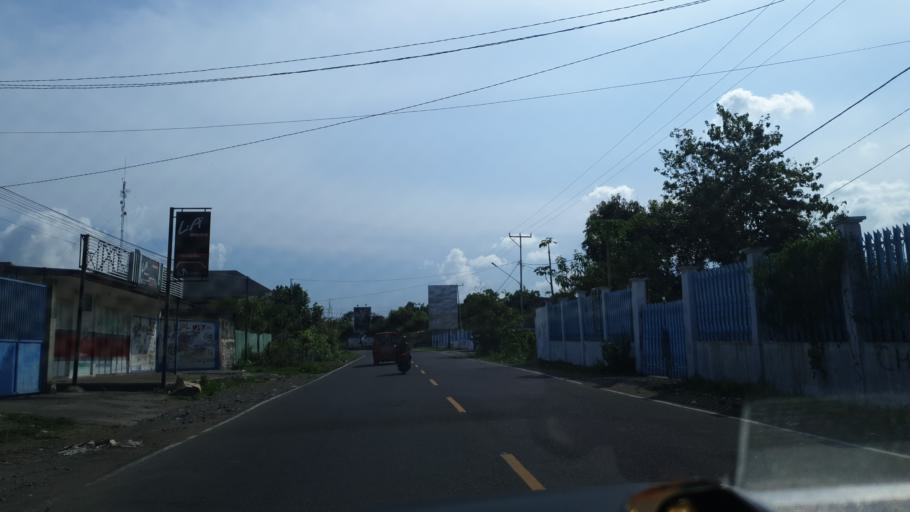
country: ID
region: East Nusa Tenggara
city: Nangalimang
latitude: -8.6352
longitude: 122.2097
